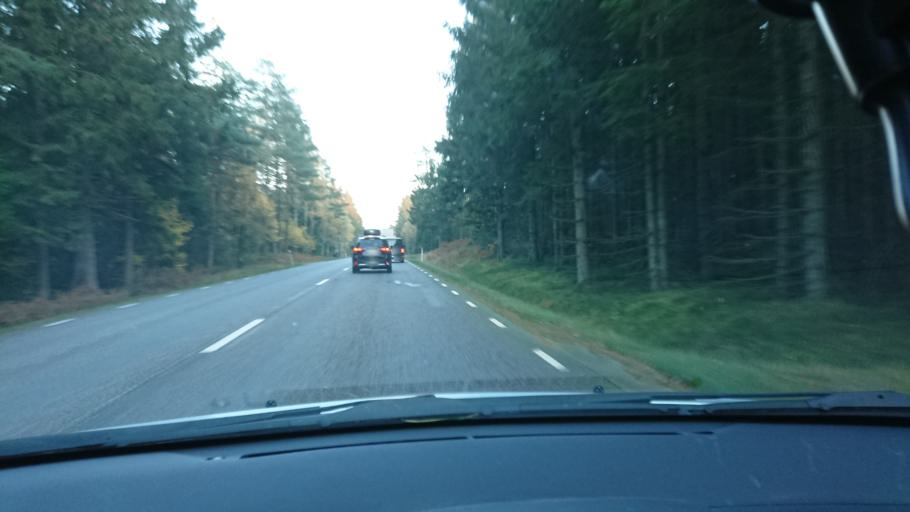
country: SE
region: Halland
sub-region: Laholms Kommun
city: Veinge
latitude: 56.7184
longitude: 13.1819
